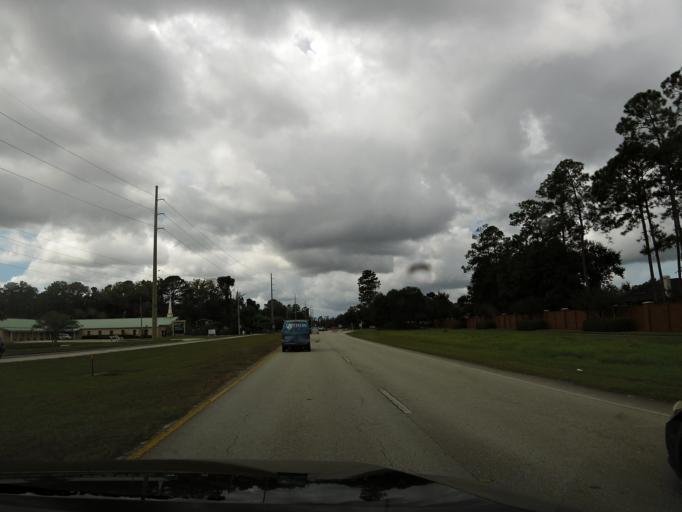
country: US
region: Florida
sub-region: Clay County
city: Lakeside
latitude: 30.1020
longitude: -81.7314
